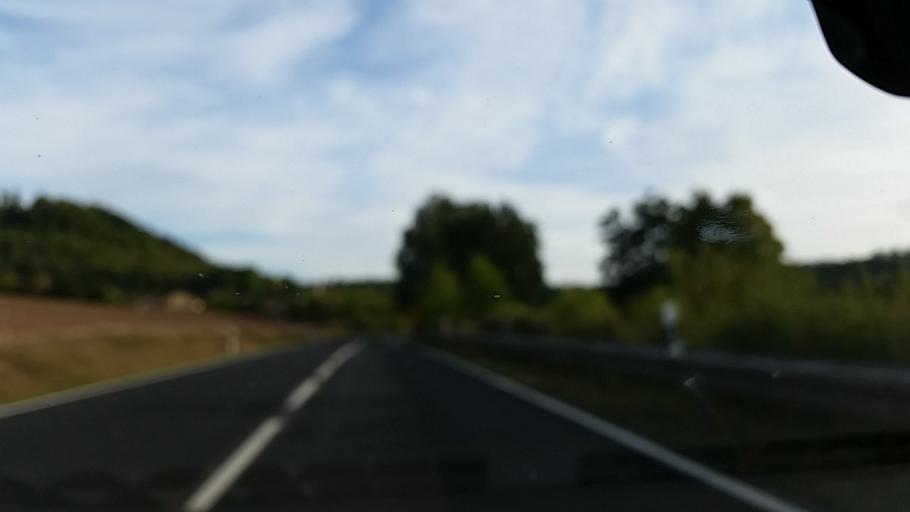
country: DE
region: Thuringia
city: Henneberg
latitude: 50.4986
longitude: 10.3555
